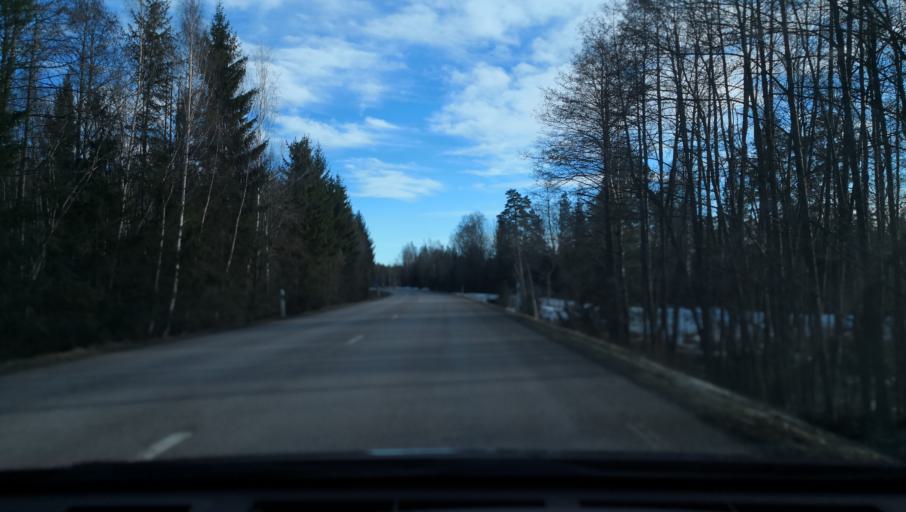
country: SE
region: Uppsala
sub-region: Osthammars Kommun
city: Osterbybruk
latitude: 60.1772
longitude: 17.9171
